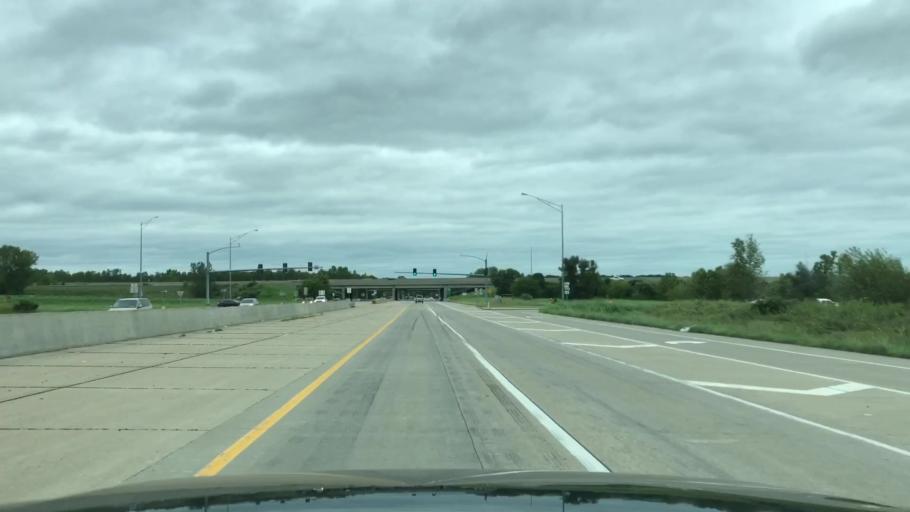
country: US
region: Missouri
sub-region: Saint Louis County
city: Maryland Heights
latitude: 38.7109
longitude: -90.5015
